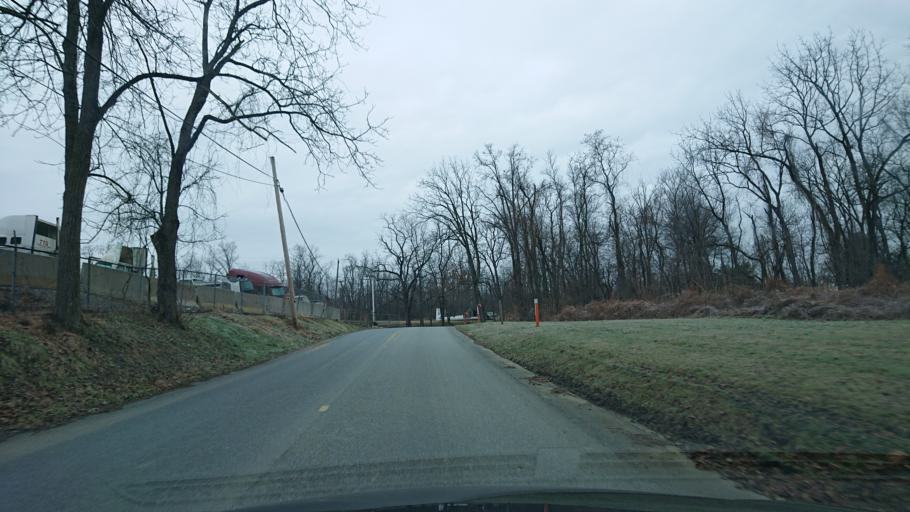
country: US
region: Pennsylvania
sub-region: Lebanon County
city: Palmyra
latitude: 40.3834
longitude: -76.6239
